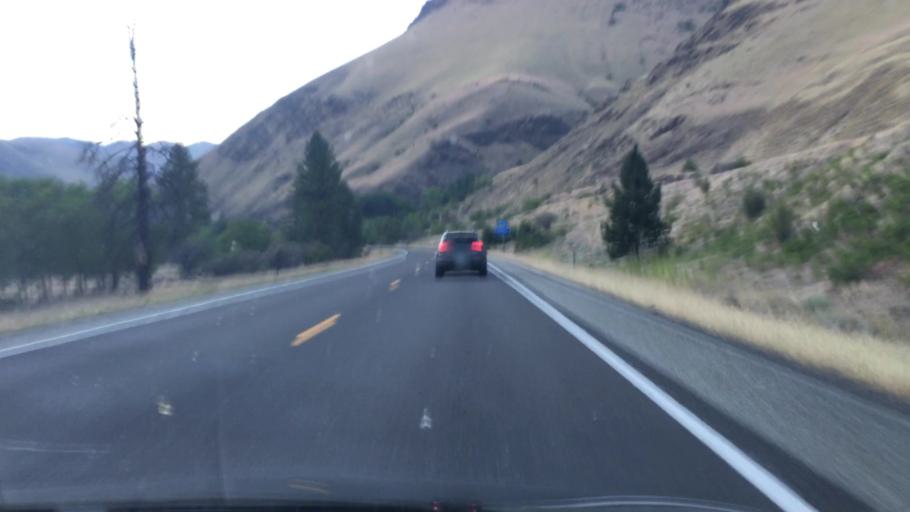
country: US
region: Idaho
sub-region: Valley County
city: McCall
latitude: 45.3369
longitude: -116.3476
